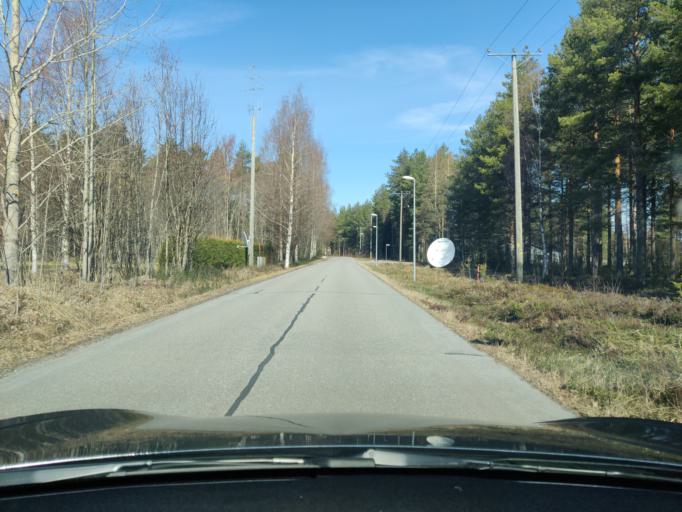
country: FI
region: Northern Savo
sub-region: Kuopio
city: Vehmersalmi
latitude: 62.7704
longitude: 27.9863
